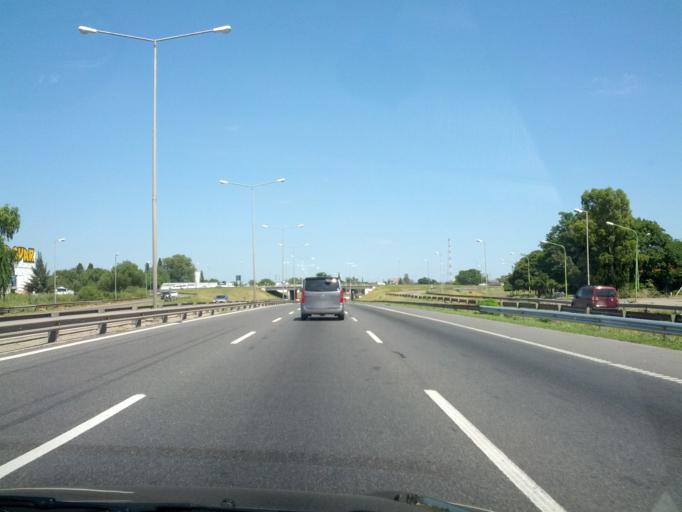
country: AR
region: Buenos Aires
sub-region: Partido de Campana
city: Campana
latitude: -34.1816
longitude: -58.9577
